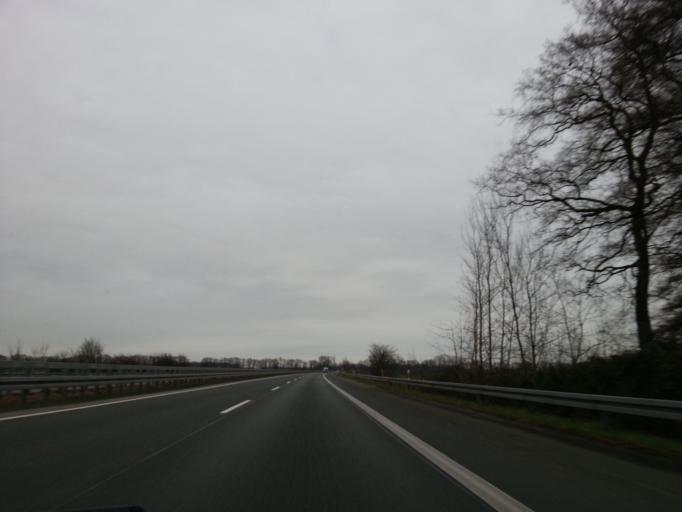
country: DE
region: North Rhine-Westphalia
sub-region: Regierungsbezirk Dusseldorf
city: Mehrhoog
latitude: 51.7733
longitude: 6.5314
